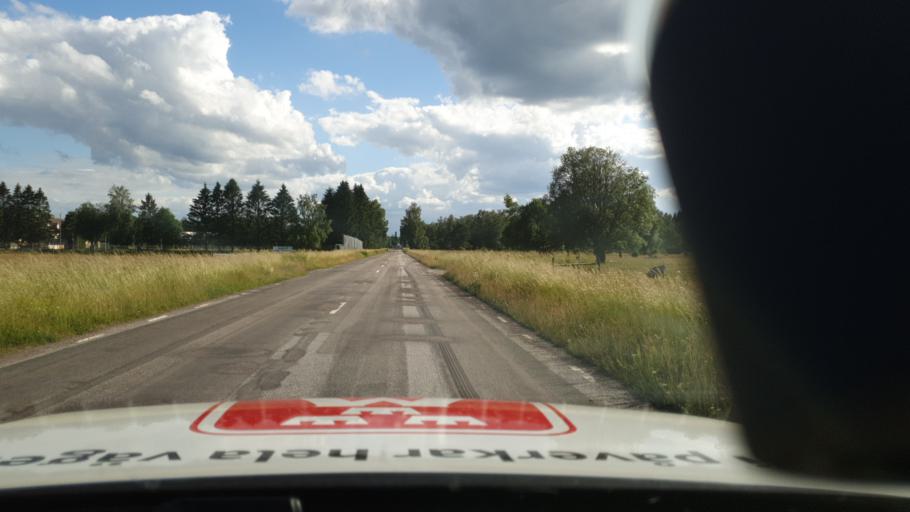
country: SE
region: Vaestra Goetaland
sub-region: Skara Kommun
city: Axvall
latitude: 58.3957
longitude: 13.5792
